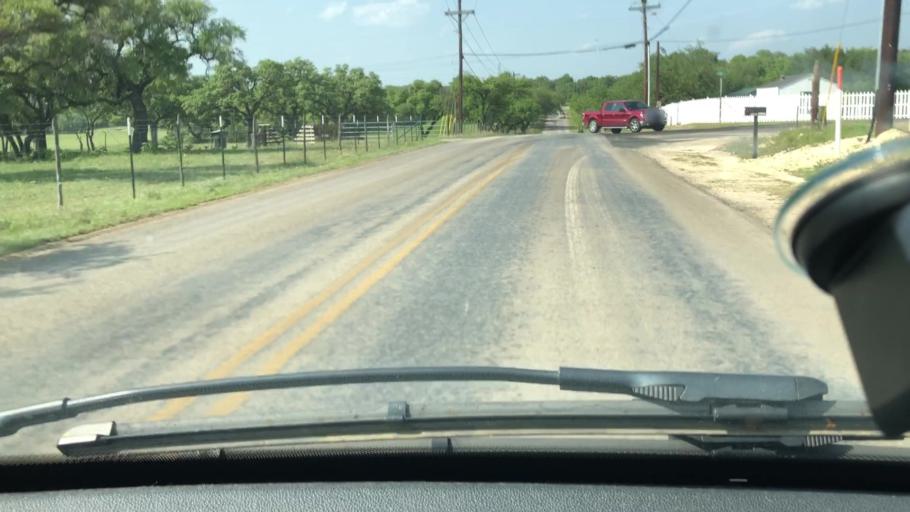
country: US
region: Texas
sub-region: Comal County
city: Bulverde
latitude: 29.7718
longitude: -98.4588
